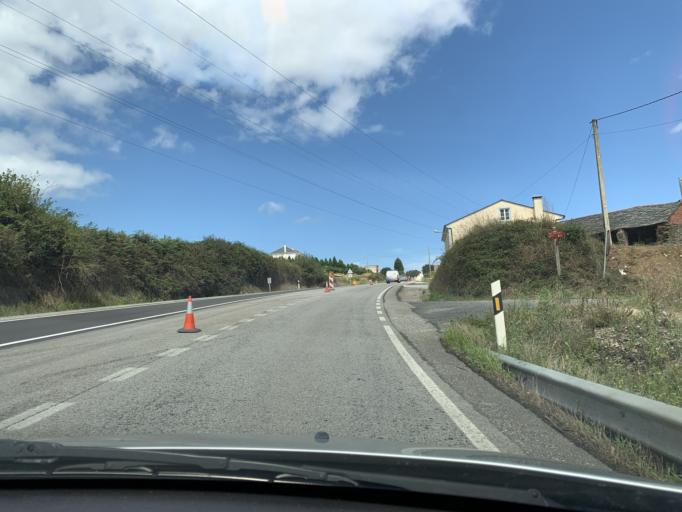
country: ES
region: Galicia
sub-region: Provincia de Lugo
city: Foz
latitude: 43.5465
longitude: -7.2707
